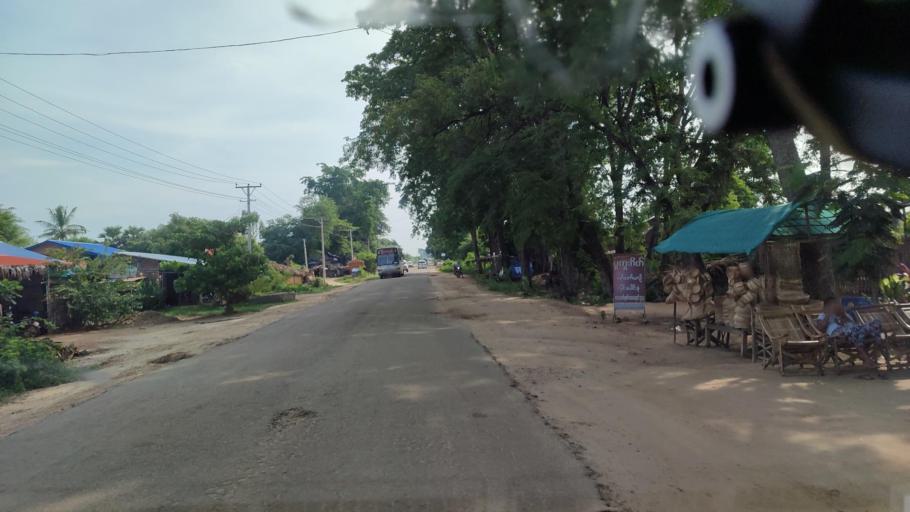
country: MM
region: Magway
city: Pakokku
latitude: 21.3307
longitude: 95.2550
